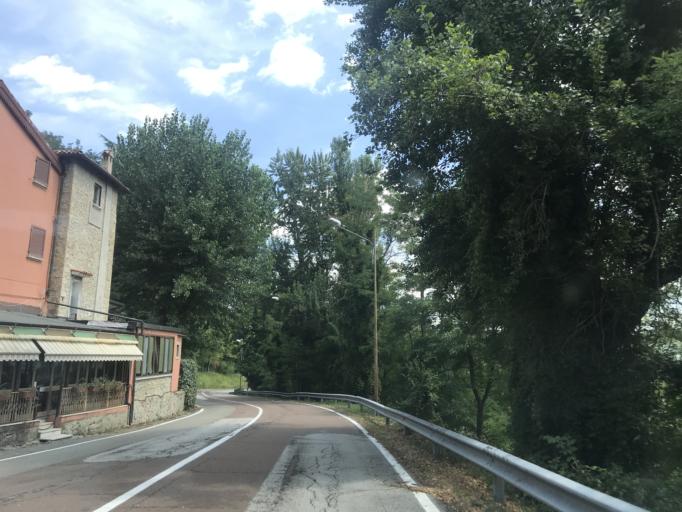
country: IT
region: Emilia-Romagna
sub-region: Provincia di Bologna
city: Grizzana
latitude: 44.2582
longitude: 11.1566
